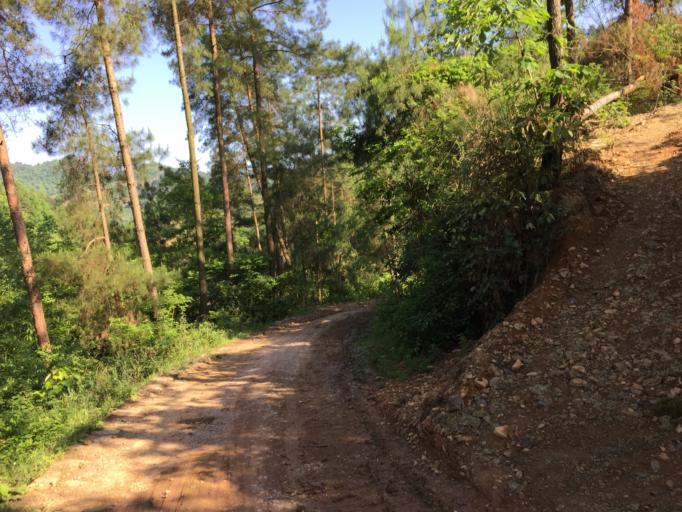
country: CN
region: Guizhou Sheng
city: Xujiaba
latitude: 27.7156
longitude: 108.0204
